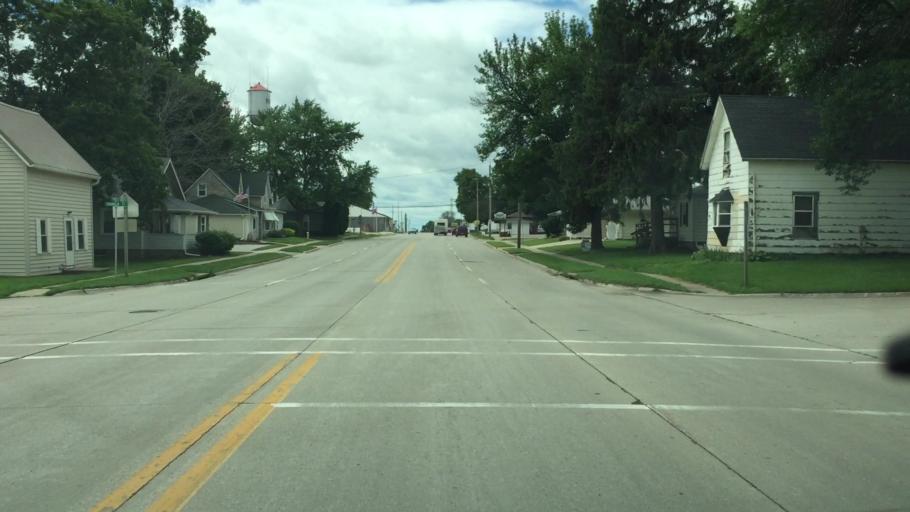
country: US
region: Iowa
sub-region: Jasper County
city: Monroe
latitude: 41.5243
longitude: -93.1018
